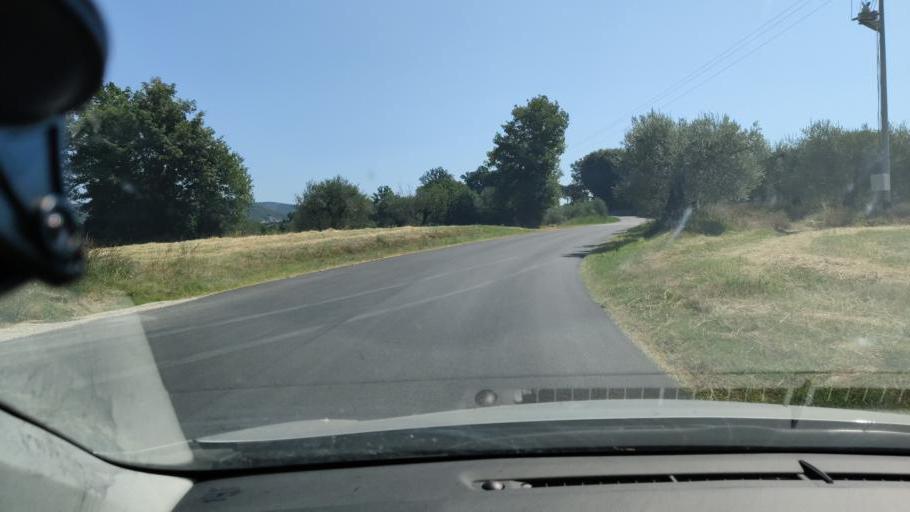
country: IT
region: Umbria
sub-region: Provincia di Terni
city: Fornole
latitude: 42.5286
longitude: 12.4438
